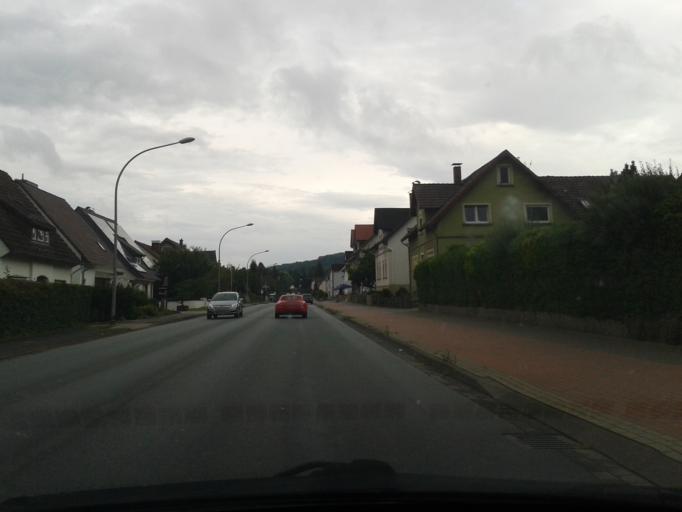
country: DE
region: North Rhine-Westphalia
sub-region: Regierungsbezirk Detmold
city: Detmold
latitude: 51.9174
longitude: 8.9040
